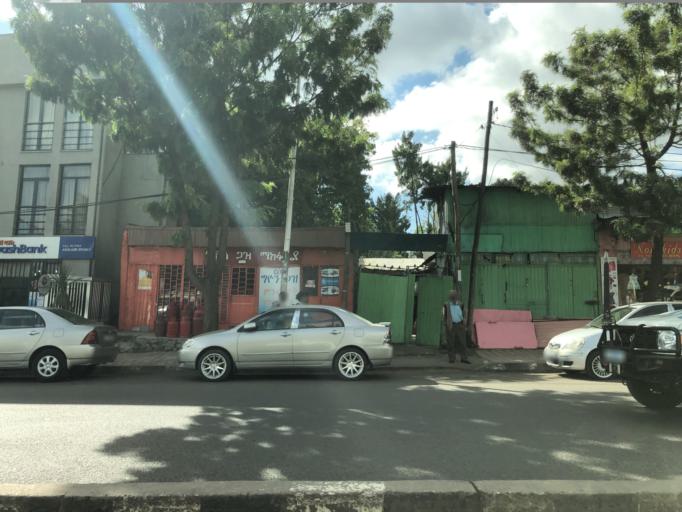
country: ET
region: Adis Abeba
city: Addis Ababa
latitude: 9.0243
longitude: 38.7766
